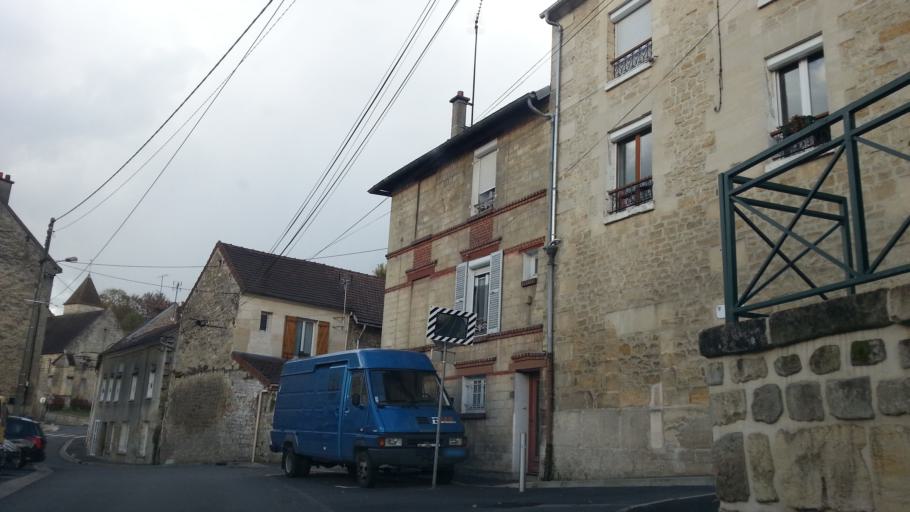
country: FR
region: Picardie
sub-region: Departement de l'Oise
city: Thiverny
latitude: 49.2561
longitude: 2.4005
